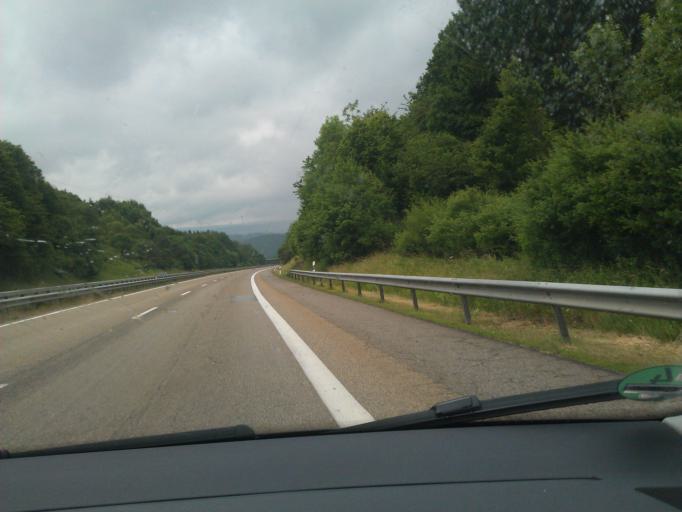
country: DE
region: Rheinland-Pfalz
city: Gimbweiler
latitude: 49.5914
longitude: 7.1978
